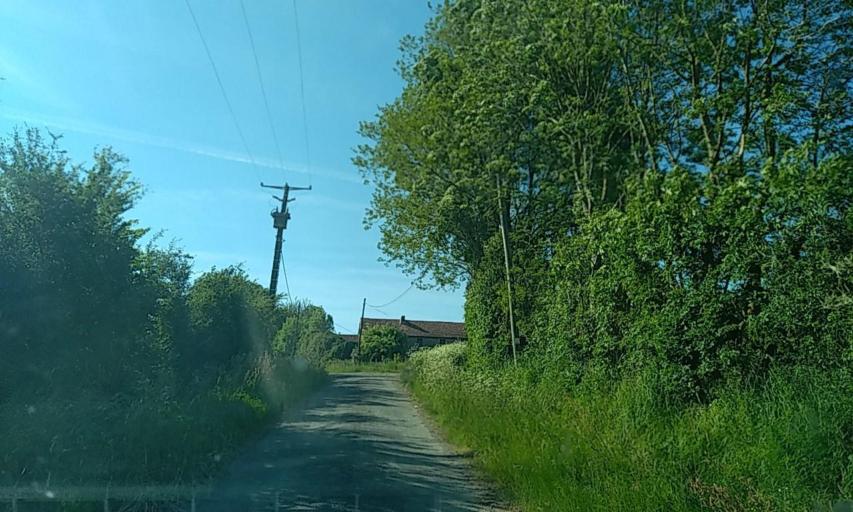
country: FR
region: Poitou-Charentes
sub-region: Departement des Deux-Sevres
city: Boisme
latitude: 46.7828
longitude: -0.4376
